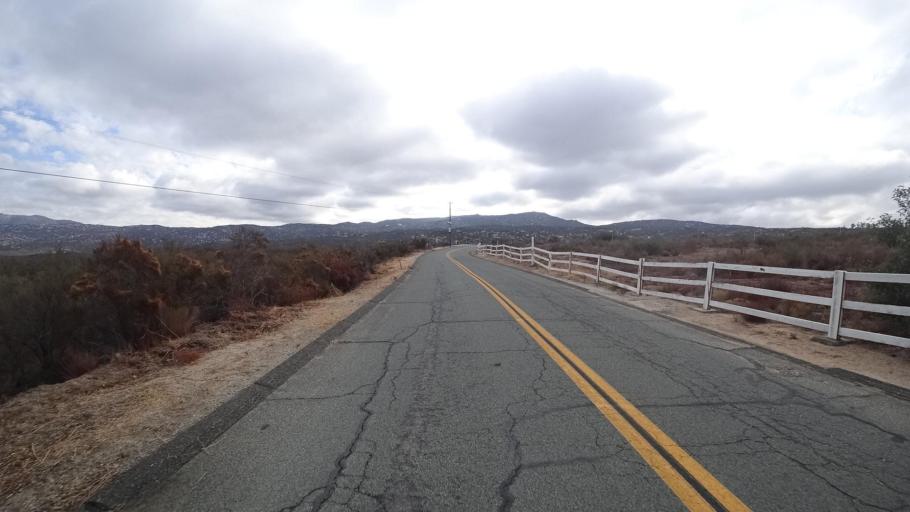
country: MX
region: Baja California
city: Tecate
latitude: 32.6299
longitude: -116.5859
